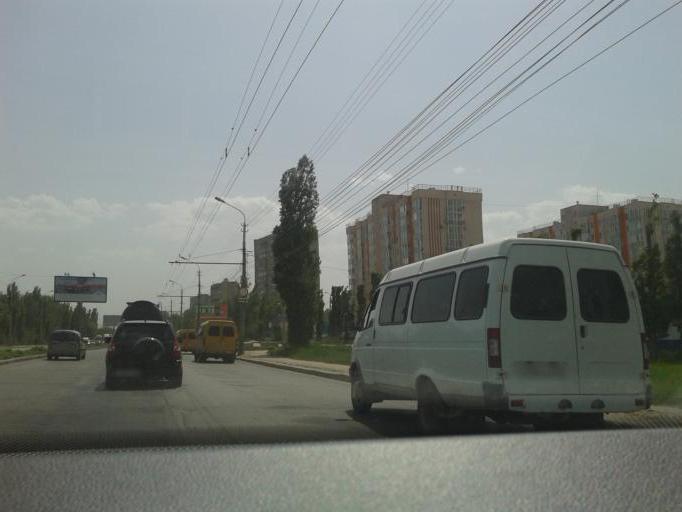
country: RU
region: Volgograd
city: Volgograd
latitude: 48.6247
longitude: 44.4259
